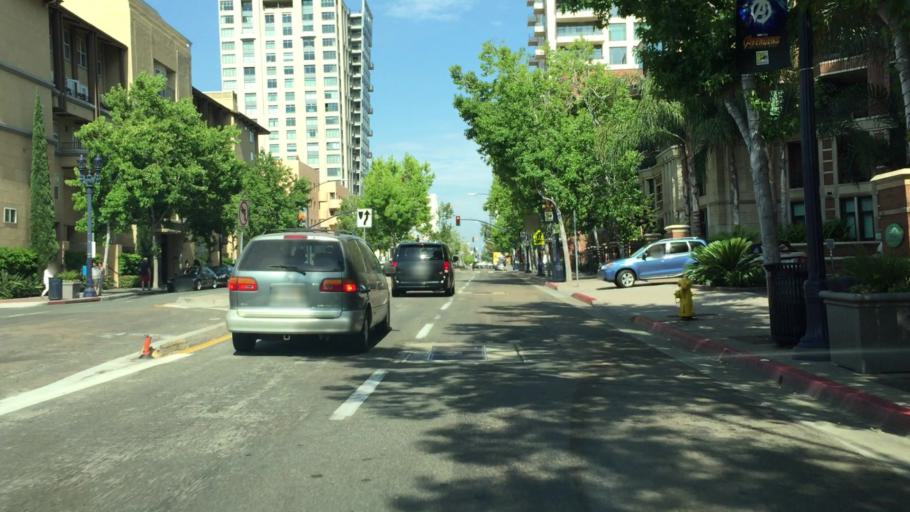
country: US
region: California
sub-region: San Diego County
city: San Diego
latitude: 32.7114
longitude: -117.1668
